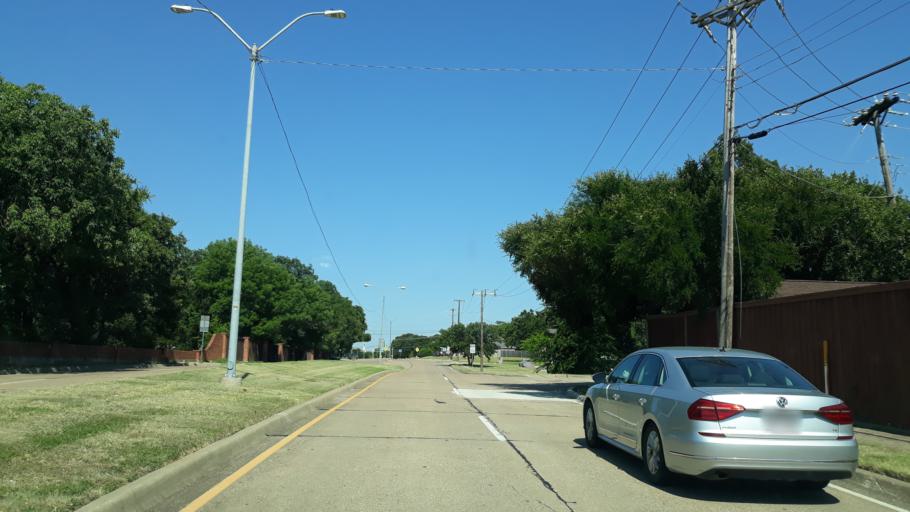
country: US
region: Texas
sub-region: Dallas County
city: Irving
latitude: 32.8216
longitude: -97.0060
